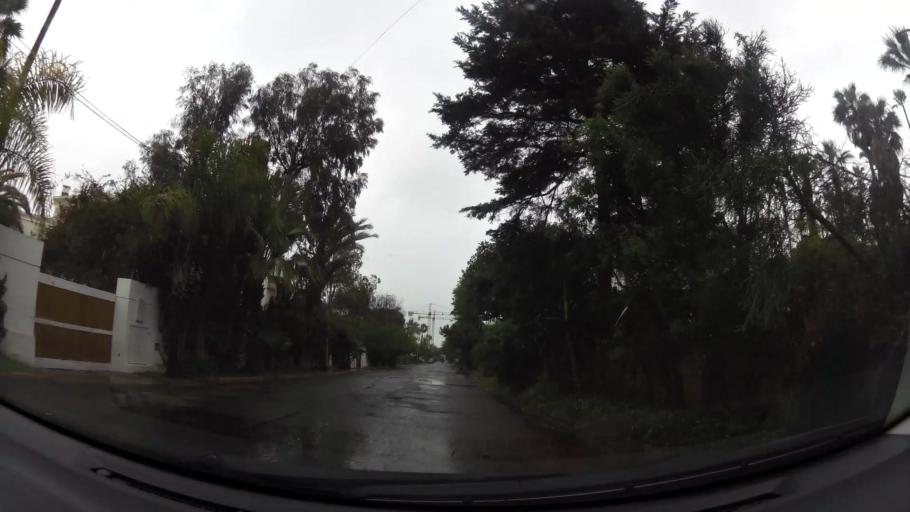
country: MA
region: Grand Casablanca
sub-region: Casablanca
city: Casablanca
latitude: 33.5871
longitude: -7.6704
